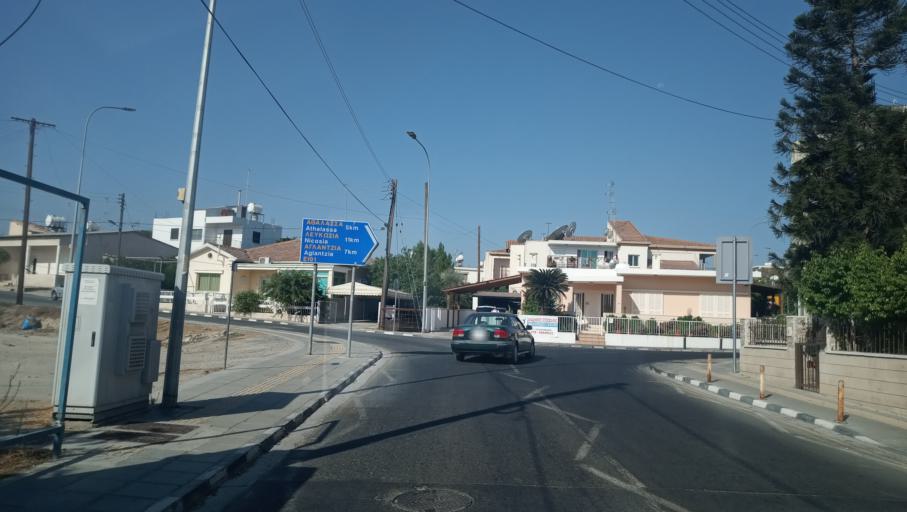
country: CY
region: Lefkosia
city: Geri
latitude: 35.1063
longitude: 33.4220
